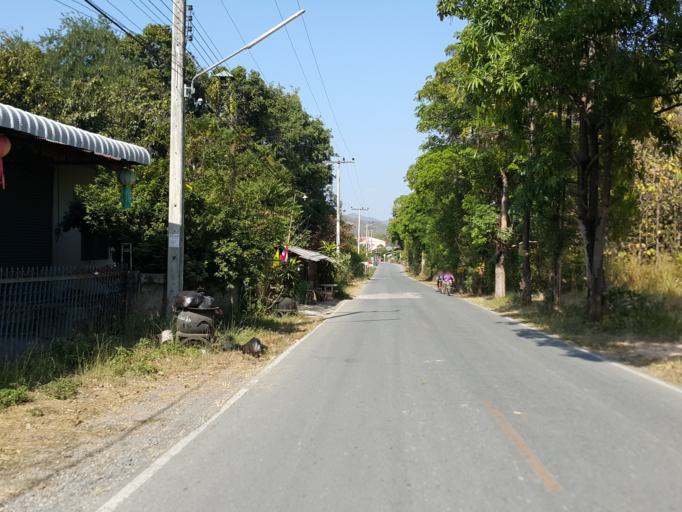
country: TH
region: Chiang Mai
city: Mae On
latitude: 18.8191
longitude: 99.1780
